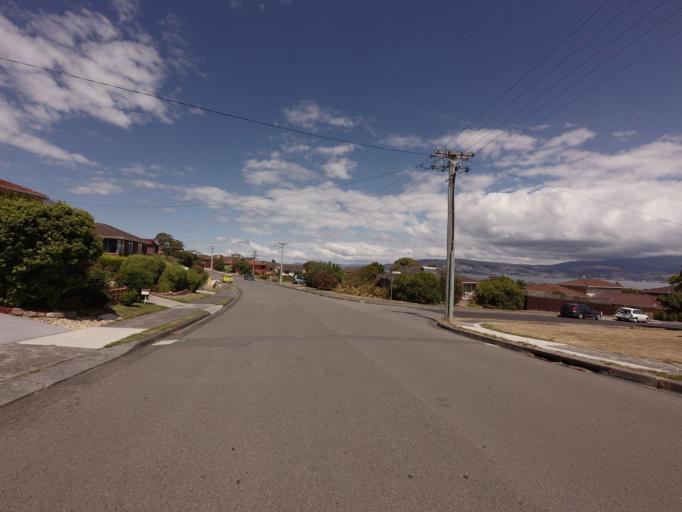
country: AU
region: Tasmania
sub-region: Clarence
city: Howrah
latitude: -42.8799
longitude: 147.4105
